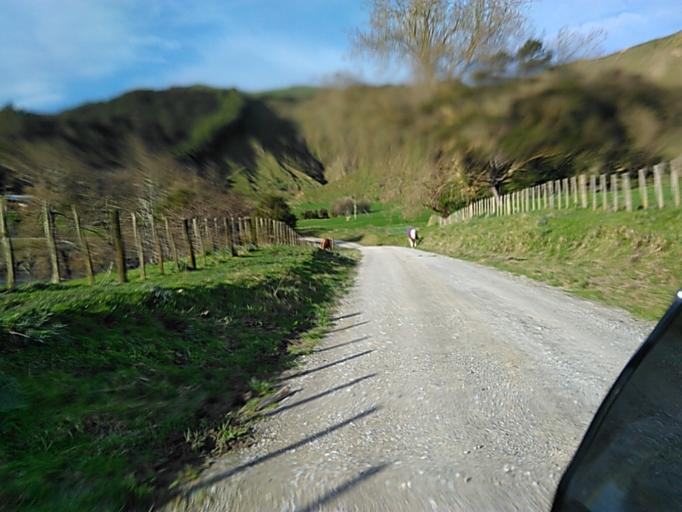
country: NZ
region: Gisborne
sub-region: Gisborne District
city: Gisborne
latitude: -38.5980
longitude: 178.0683
